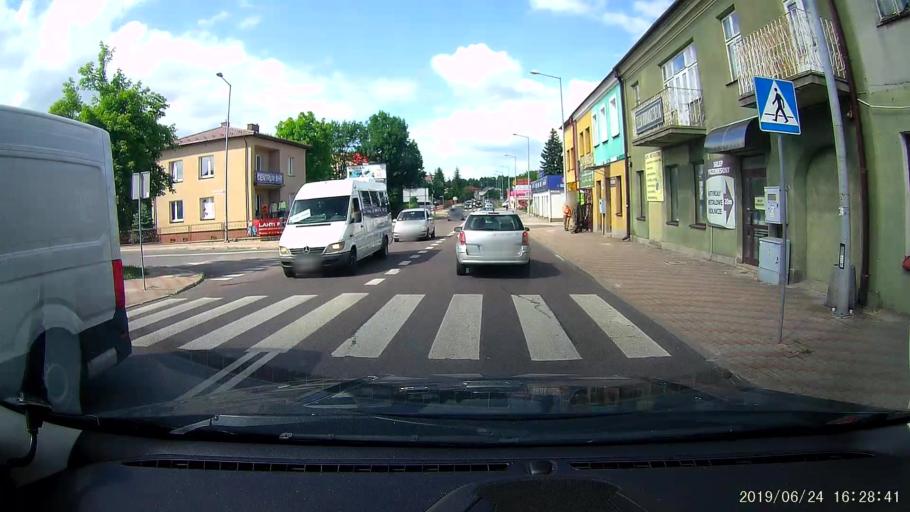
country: PL
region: Lublin Voivodeship
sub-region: Powiat tomaszowski
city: Tomaszow Lubelski
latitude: 50.4550
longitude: 23.4201
